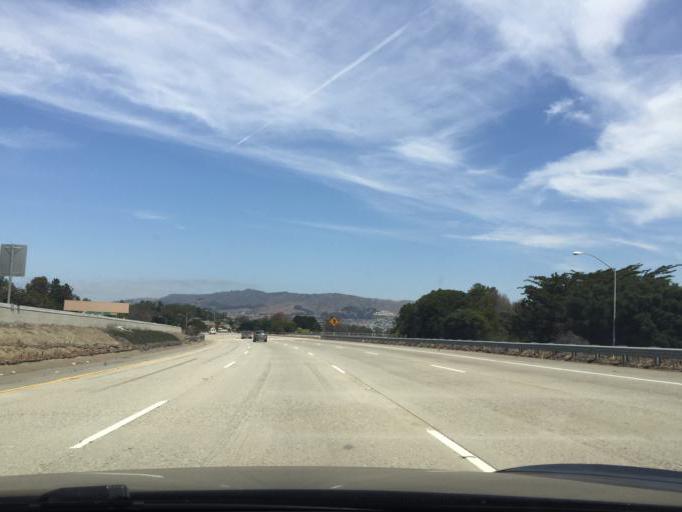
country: US
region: California
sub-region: San Mateo County
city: San Bruno
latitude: 37.6165
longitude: -122.4241
